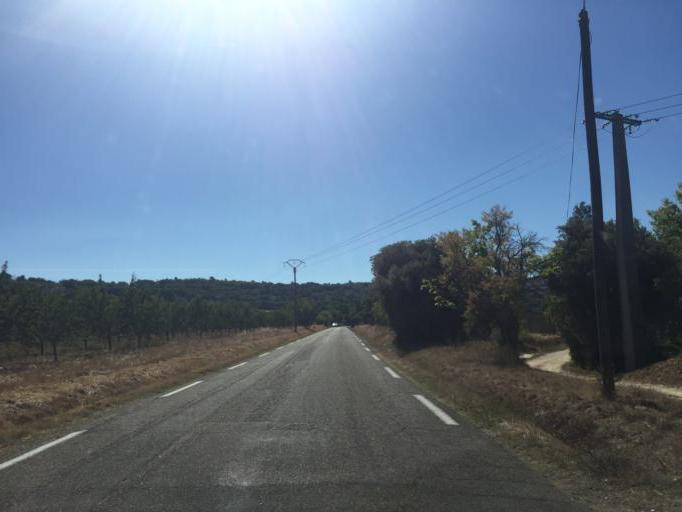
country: FR
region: Provence-Alpes-Cote d'Azur
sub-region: Departement du Vaucluse
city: Venasque
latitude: 44.0126
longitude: 5.1378
